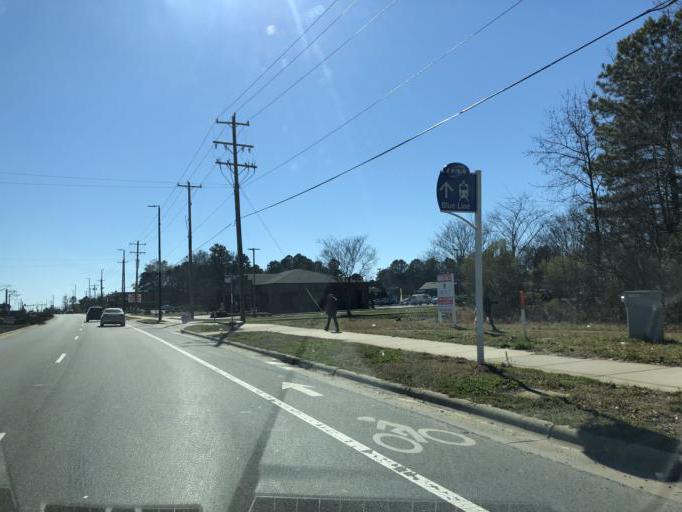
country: US
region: North Carolina
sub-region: Mecklenburg County
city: Charlotte
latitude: 35.2807
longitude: -80.7657
